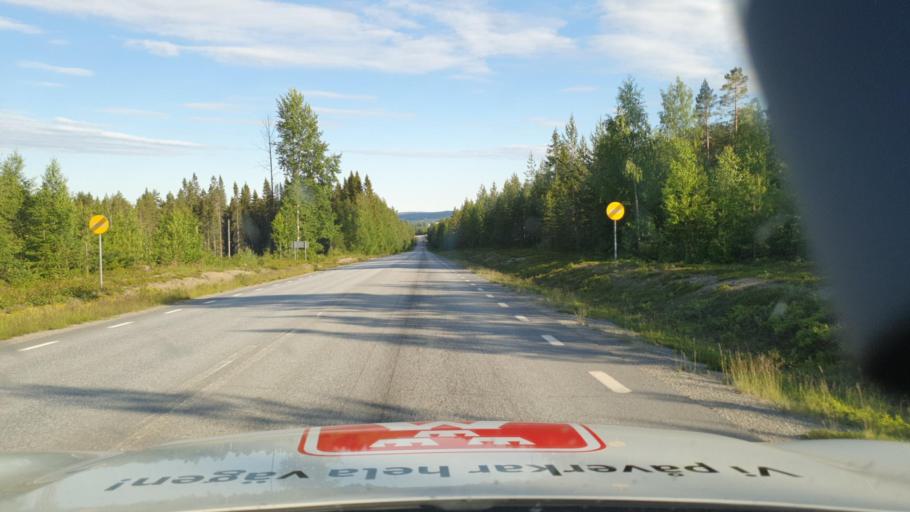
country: SE
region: Vaesterbotten
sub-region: Vannas Kommun
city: Vannasby
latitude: 64.0430
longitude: 20.0039
